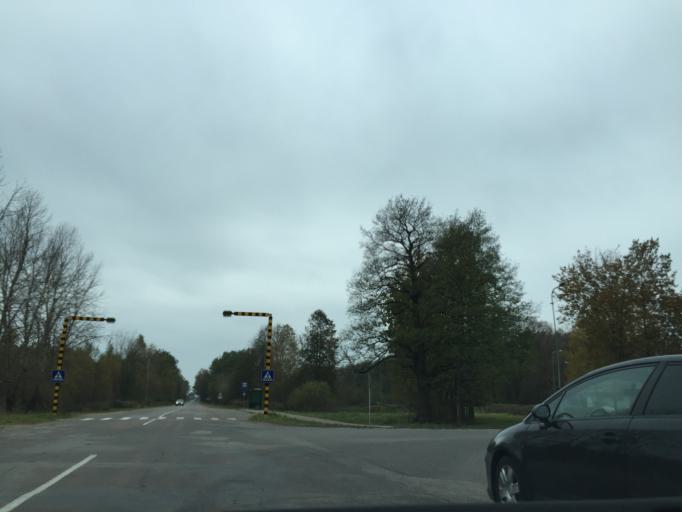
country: LV
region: Marupe
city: Marupe
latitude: 56.8544
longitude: 24.0556
